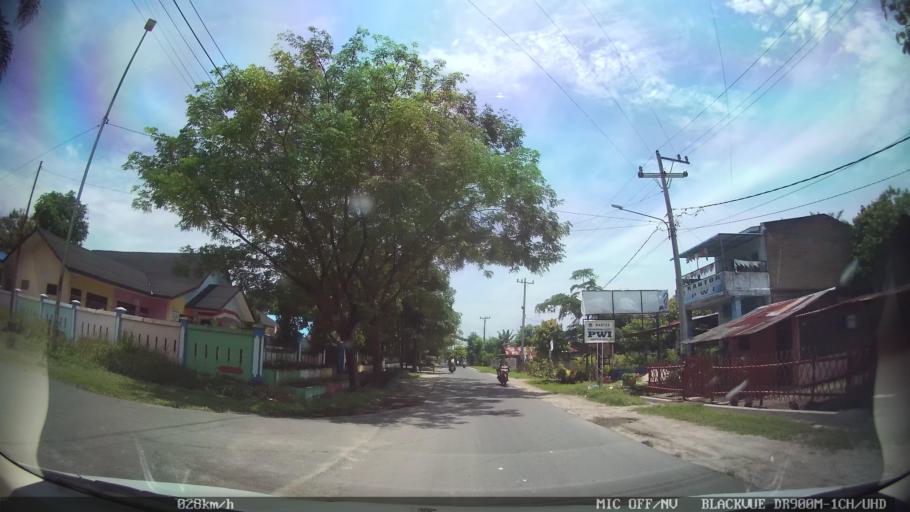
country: ID
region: North Sumatra
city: Percut
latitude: 3.5404
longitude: 98.8742
